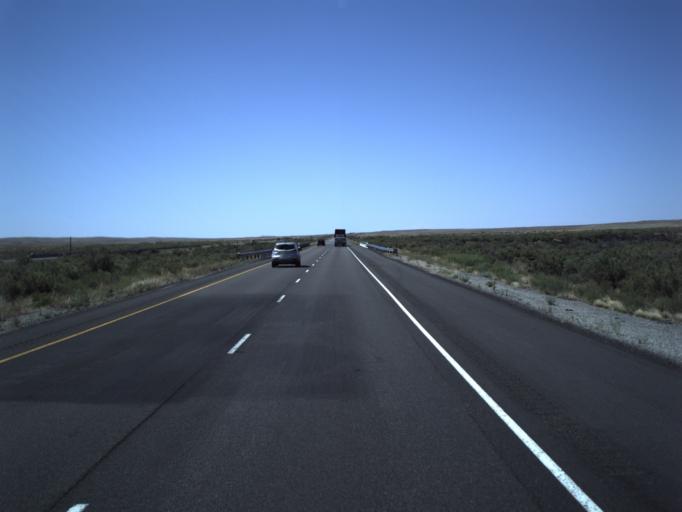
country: US
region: Colorado
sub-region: Mesa County
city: Loma
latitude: 39.0827
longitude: -109.2243
